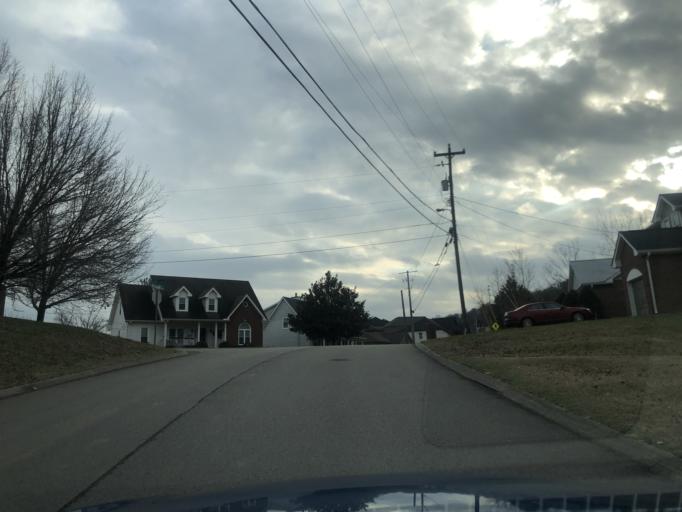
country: US
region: Tennessee
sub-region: Davidson County
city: Belle Meade
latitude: 36.1044
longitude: -86.9359
